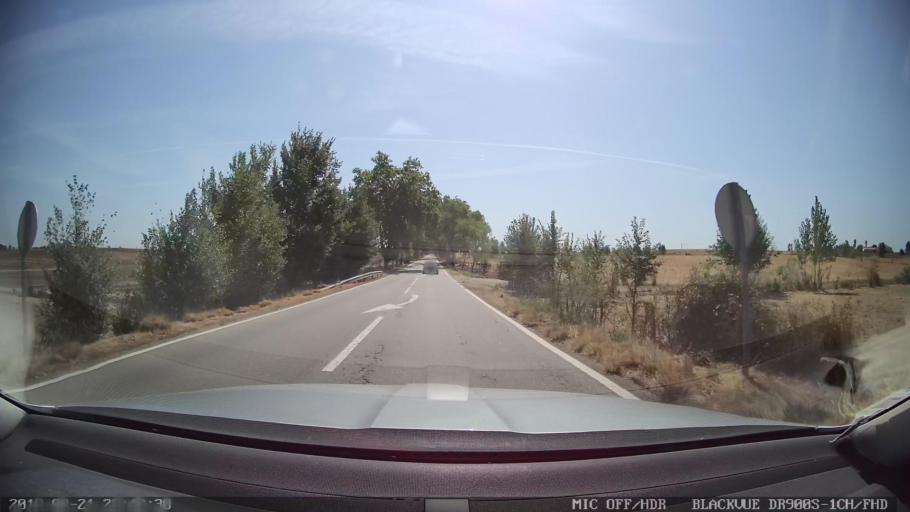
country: PT
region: Castelo Branco
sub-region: Idanha-A-Nova
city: Idanha-a-Nova
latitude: 39.8557
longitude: -7.3110
